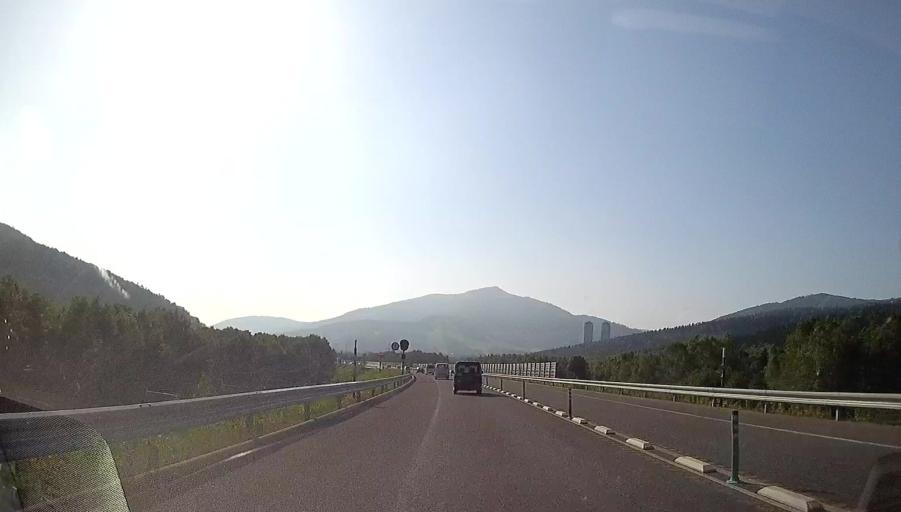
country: JP
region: Hokkaido
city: Shimo-furano
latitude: 43.0516
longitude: 142.6469
